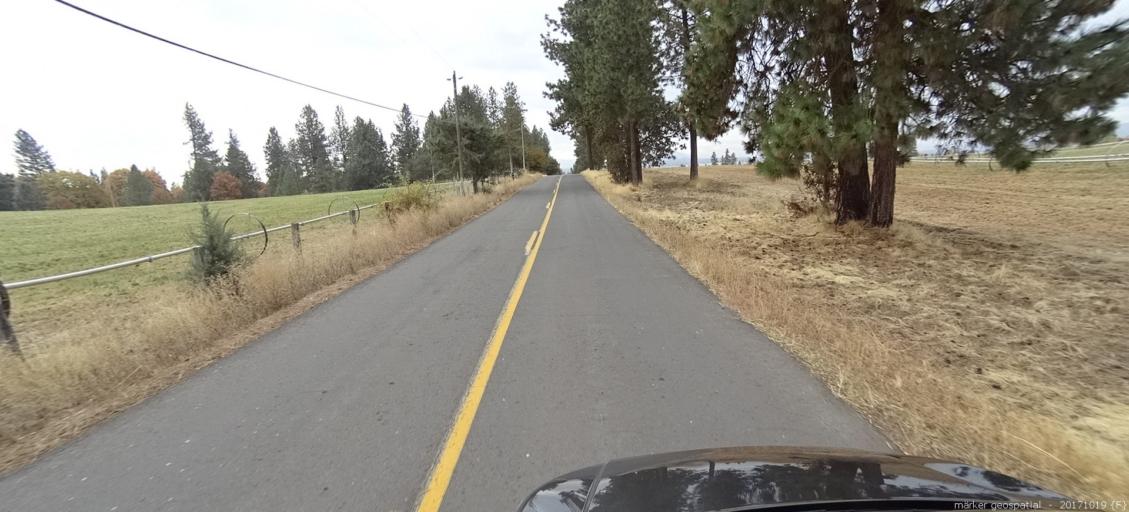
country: US
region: California
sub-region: Shasta County
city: Burney
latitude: 41.0563
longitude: -121.3410
